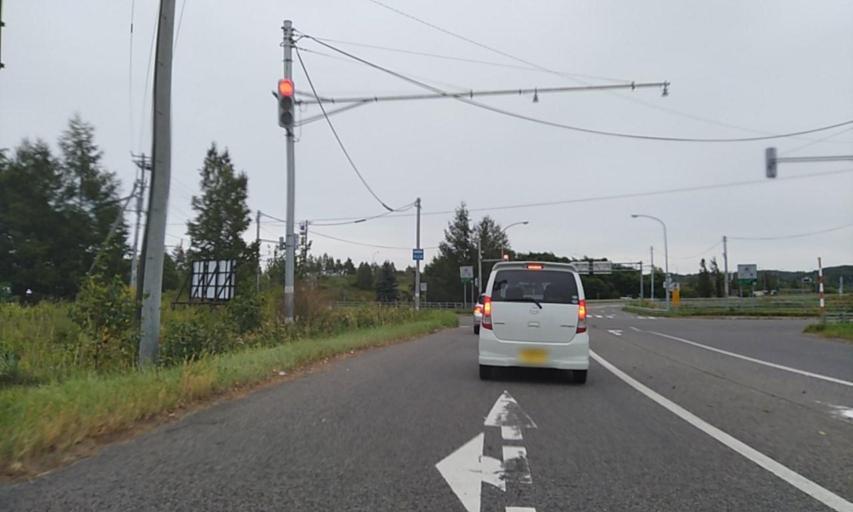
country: JP
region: Hokkaido
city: Bihoro
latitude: 43.8469
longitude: 144.1171
